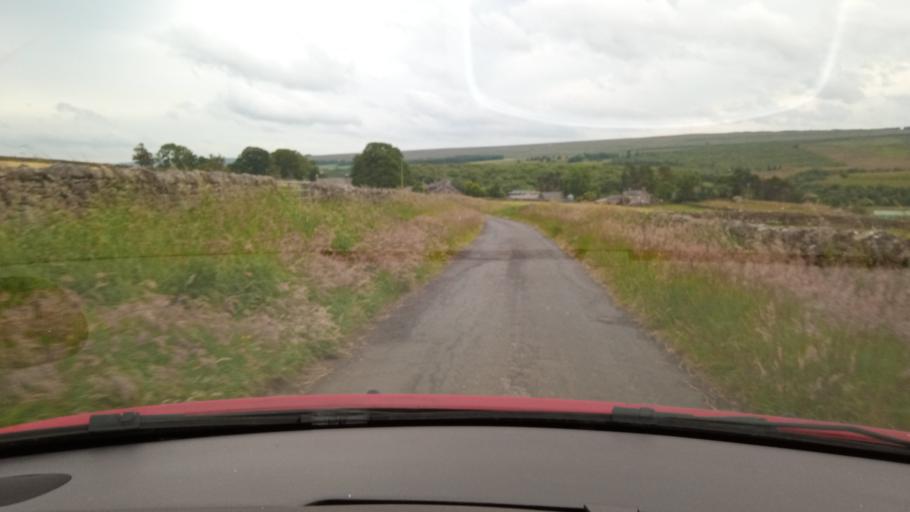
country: GB
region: England
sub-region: Northumberland
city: Rochester
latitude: 55.2799
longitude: -2.2650
